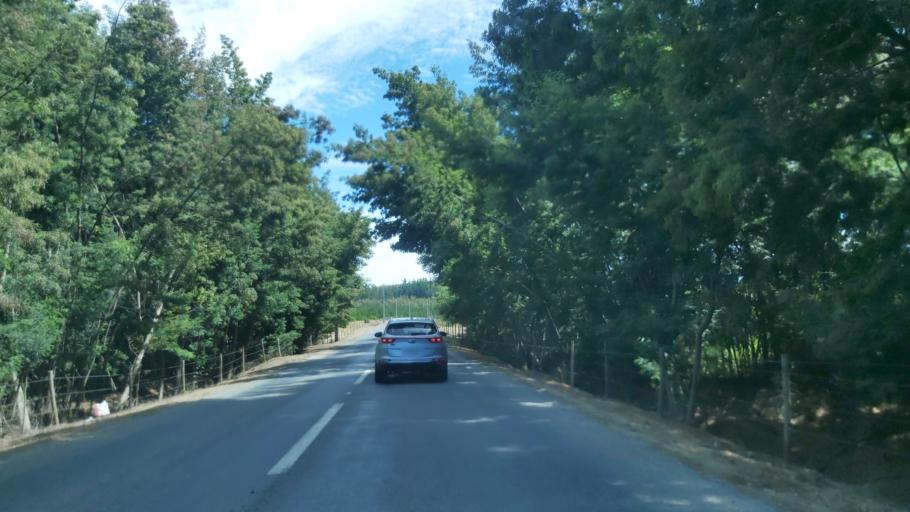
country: CL
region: Maule
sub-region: Provincia de Talca
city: Constitucion
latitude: -35.5348
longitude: -72.5449
